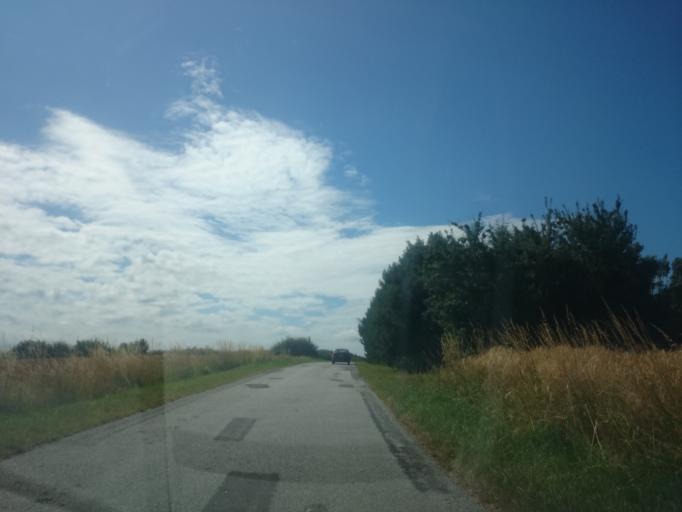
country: DK
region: South Denmark
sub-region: Langeland Kommune
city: Rudkobing
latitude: 54.9626
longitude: 10.8299
